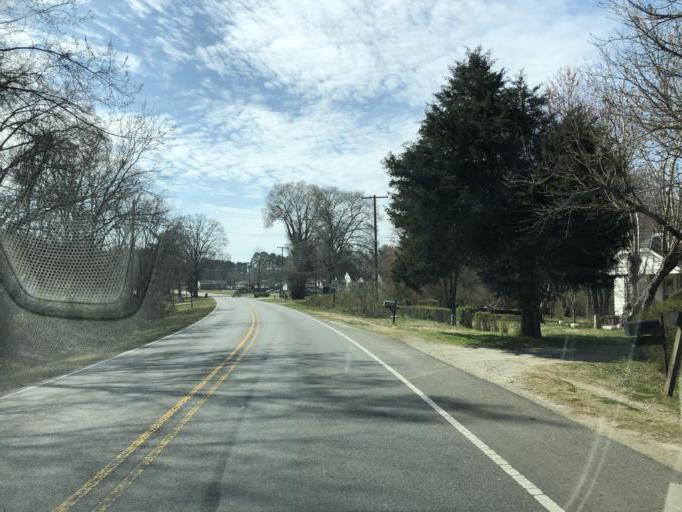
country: US
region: North Carolina
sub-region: Gaston County
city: Stanley
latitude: 35.3441
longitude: -81.1024
